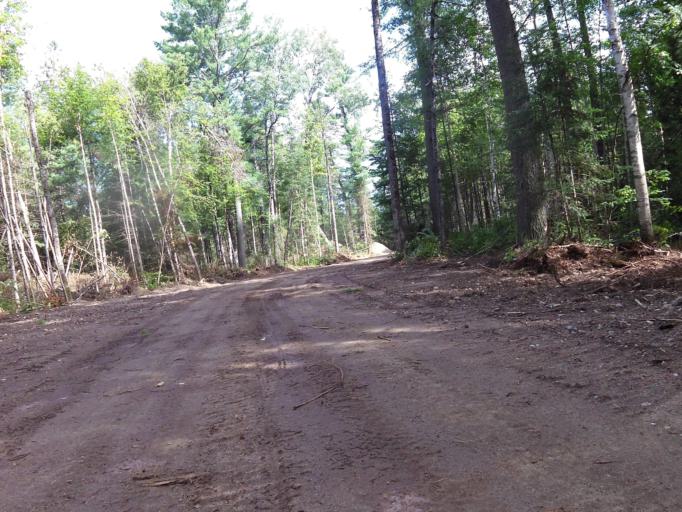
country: CA
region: Ontario
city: Renfrew
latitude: 45.1095
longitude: -76.7247
